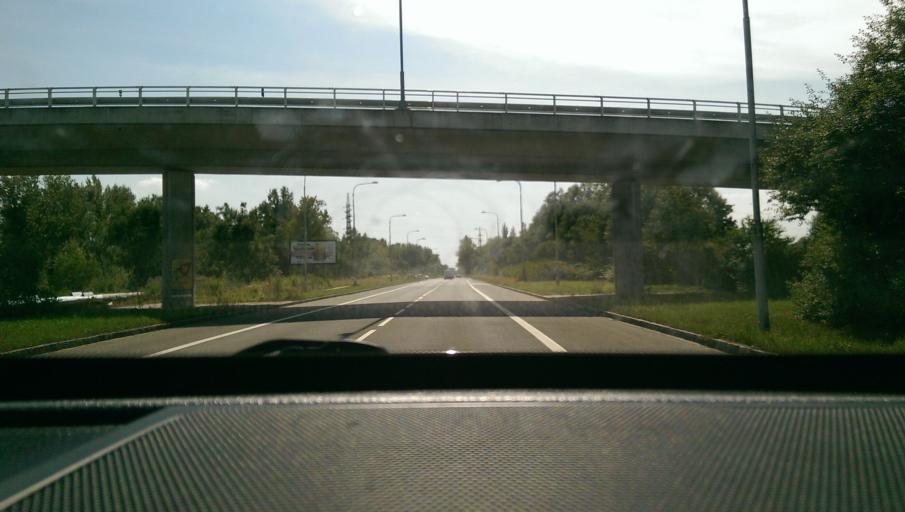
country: CZ
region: Moravskoslezsky
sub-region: Okres Ostrava-Mesto
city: Ostrava
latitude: 49.8544
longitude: 18.2548
